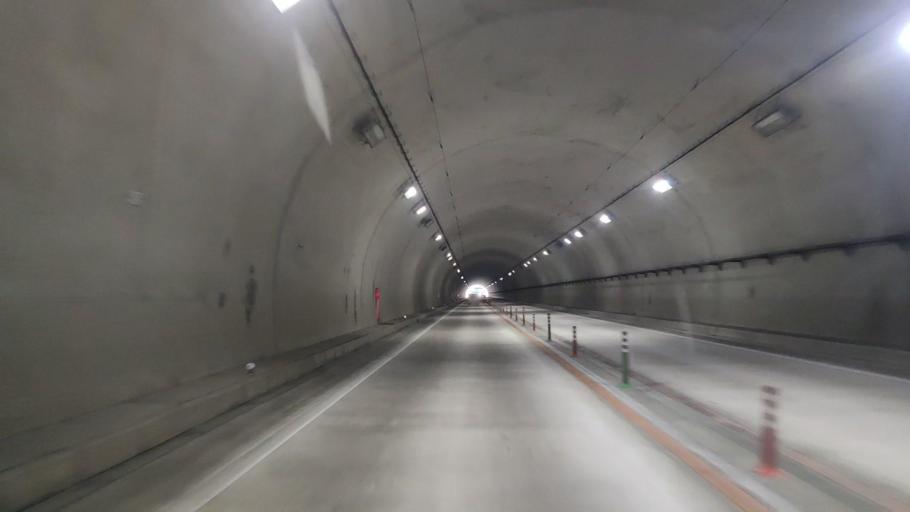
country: JP
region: Wakayama
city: Shingu
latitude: 33.6249
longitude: 135.9203
